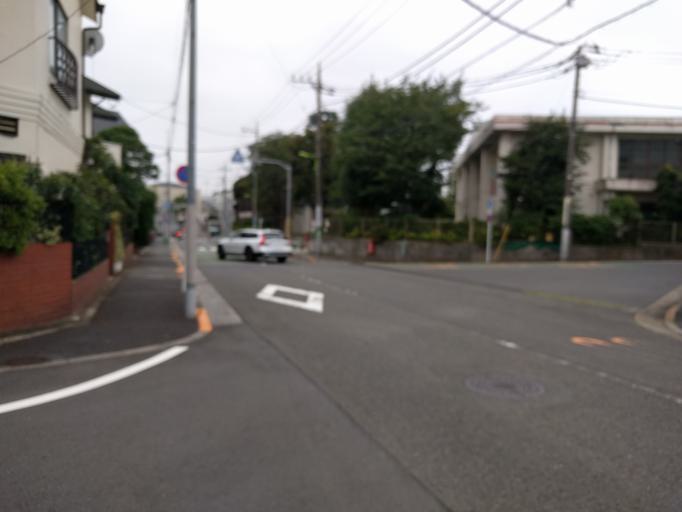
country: JP
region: Tokyo
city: Tokyo
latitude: 35.6106
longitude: 139.6447
